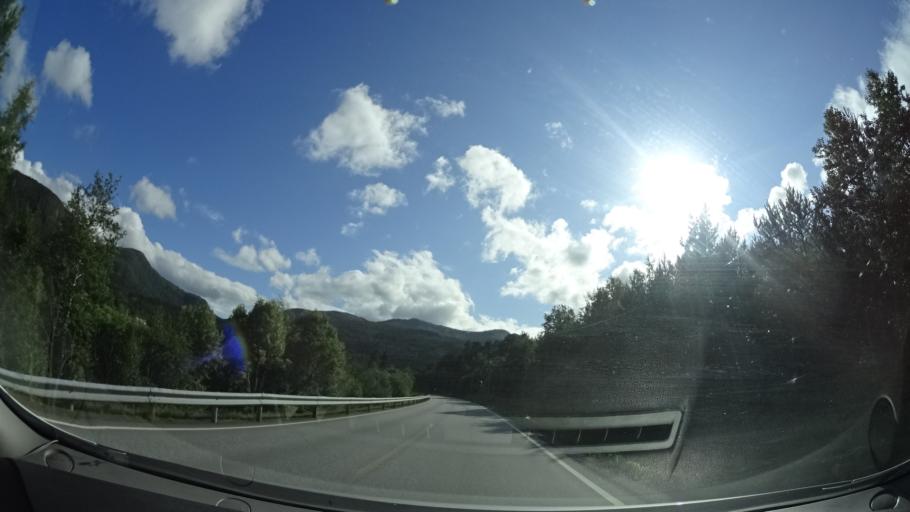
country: NO
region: More og Romsdal
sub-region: Aure
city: Aure
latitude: 63.1376
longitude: 8.5267
